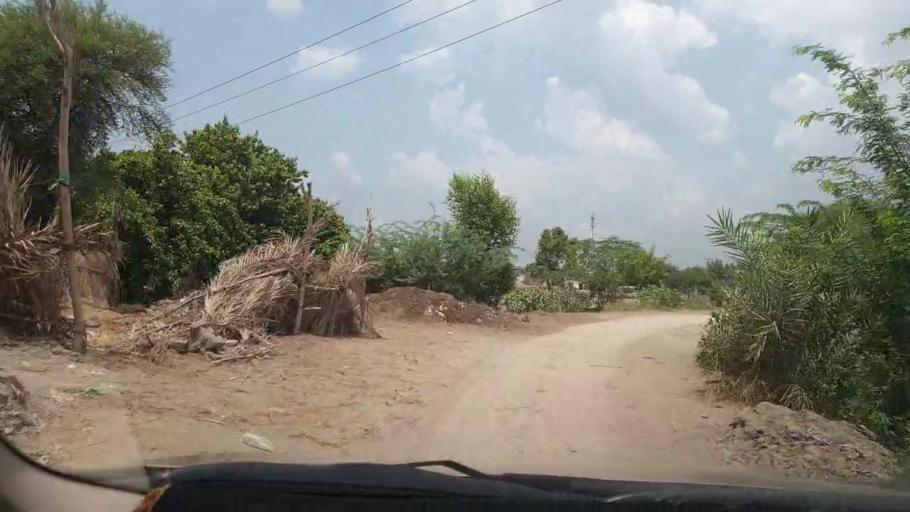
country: PK
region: Sindh
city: Larkana
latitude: 27.5755
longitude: 68.1219
